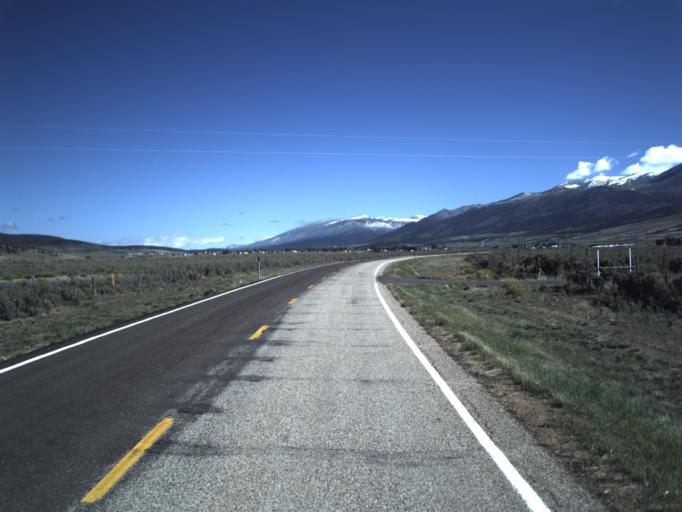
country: US
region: Utah
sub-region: Sevier County
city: Monroe
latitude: 38.4732
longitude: -111.9039
